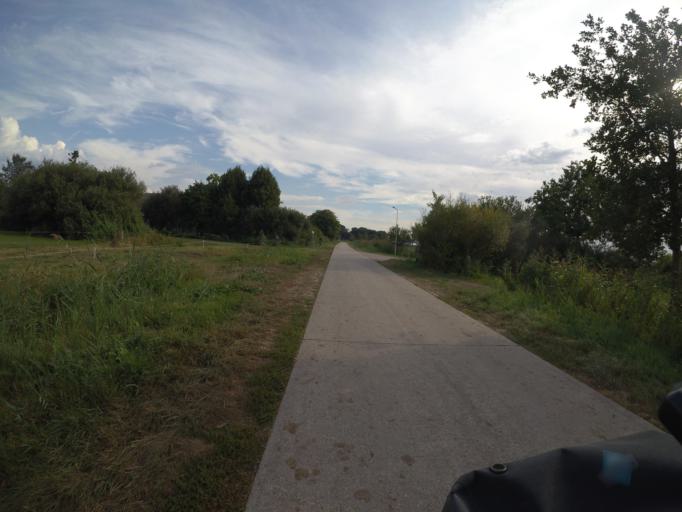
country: NL
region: Overijssel
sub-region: Gemeente Zwartewaterland
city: Hasselt
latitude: 52.6264
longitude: 6.1040
